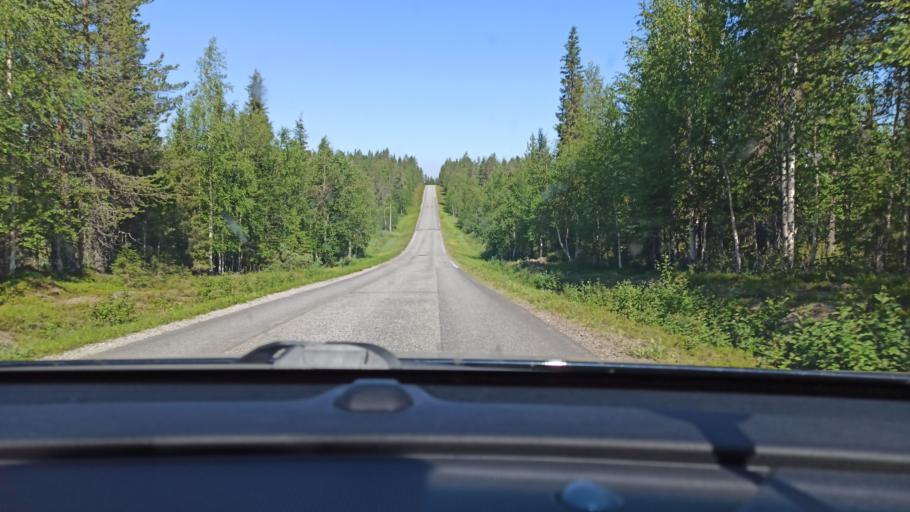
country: FI
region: Lapland
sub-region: Tunturi-Lappi
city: Kolari
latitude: 67.6767
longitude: 24.1429
